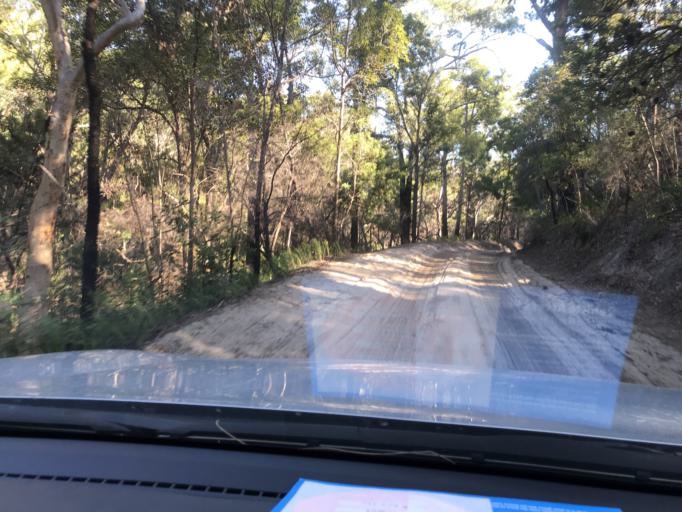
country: AU
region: Queensland
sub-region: Fraser Coast
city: Urangan
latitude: -25.5029
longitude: 153.1075
